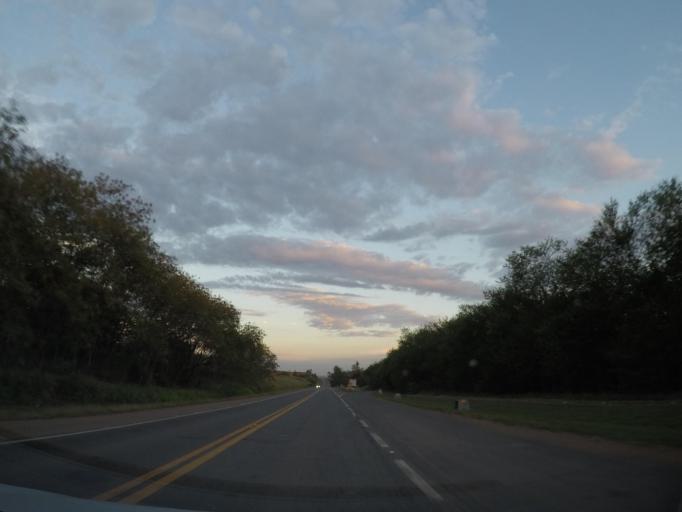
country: BR
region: Sao Paulo
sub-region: Vinhedo
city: Vinhedo
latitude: -23.0509
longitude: -47.0769
